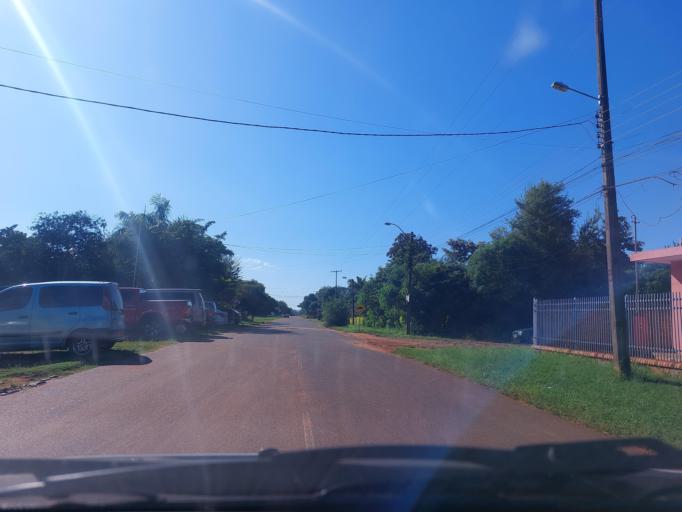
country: PY
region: San Pedro
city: Guayaybi
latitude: -24.5309
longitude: -56.4020
